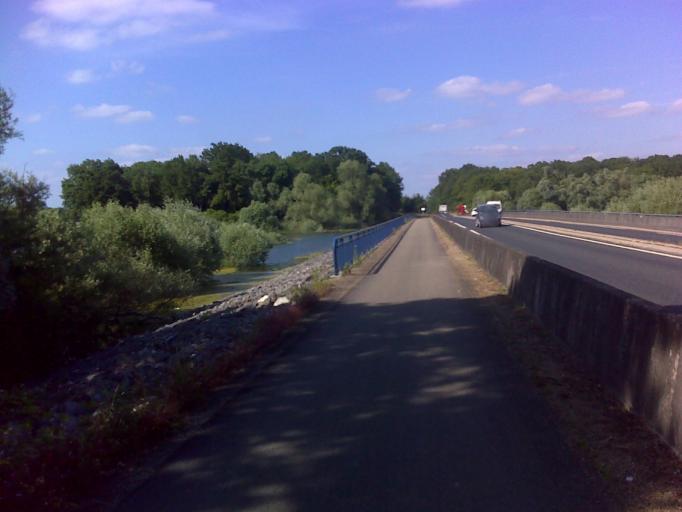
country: FR
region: Champagne-Ardenne
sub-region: Departement de la Haute-Marne
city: Villiers-en-Lieu
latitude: 48.5741
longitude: 4.8507
